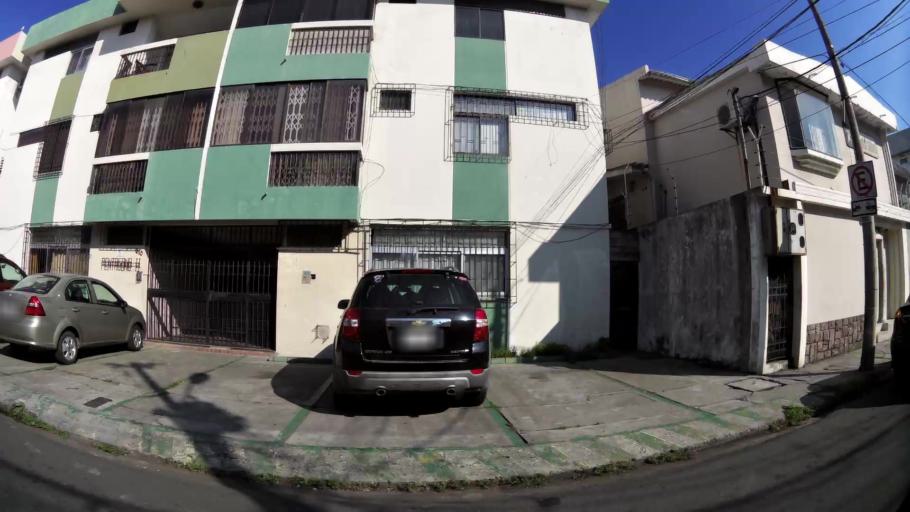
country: EC
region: Guayas
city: Guayaquil
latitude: -2.1725
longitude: -79.9006
